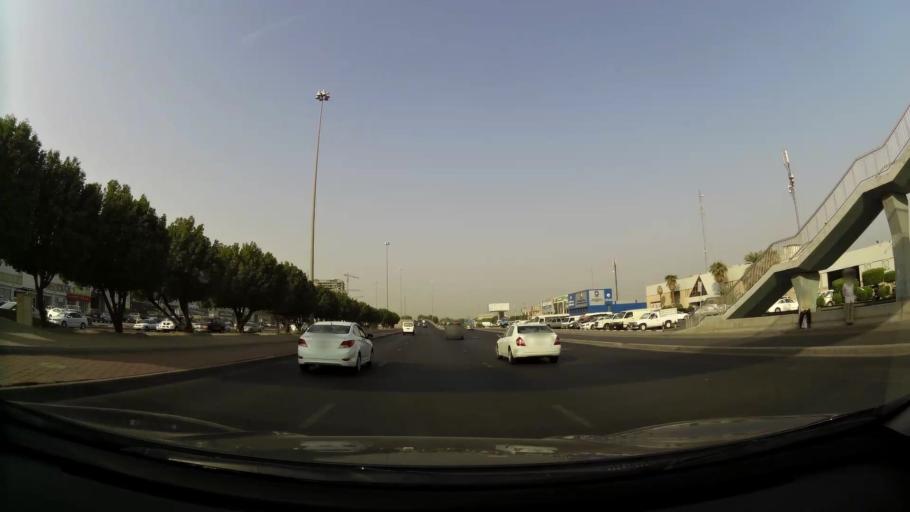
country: KW
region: Al Asimah
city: Ar Rabiyah
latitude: 29.3137
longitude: 47.9310
